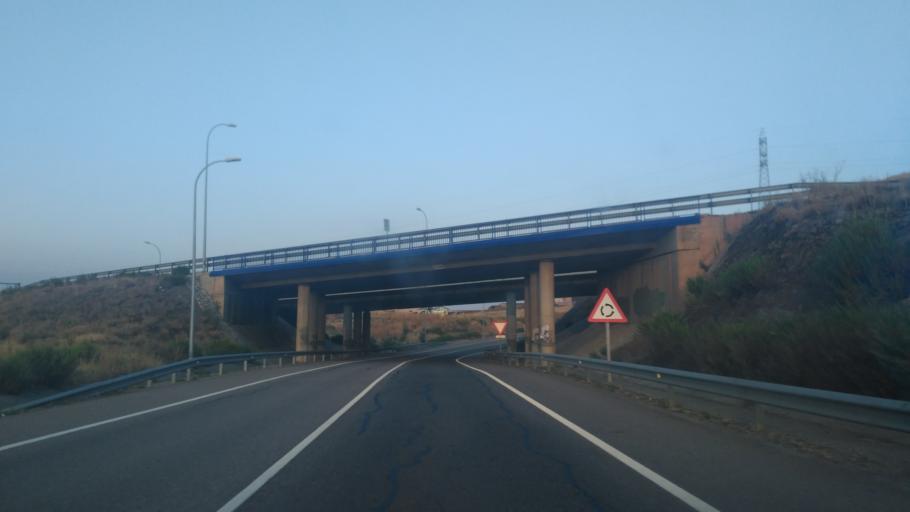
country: ES
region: Castille and Leon
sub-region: Provincia de Salamanca
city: Villamayor
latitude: 40.9626
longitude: -5.7007
